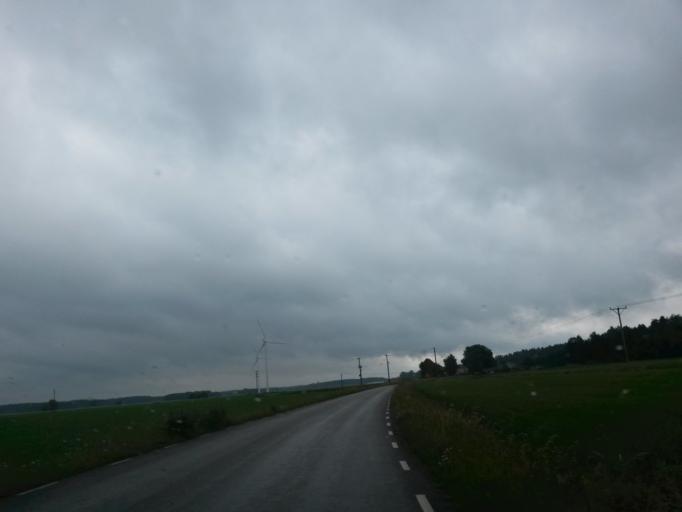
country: SE
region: Vaestra Goetaland
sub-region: Grastorps Kommun
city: Graestorp
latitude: 58.3033
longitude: 12.7820
